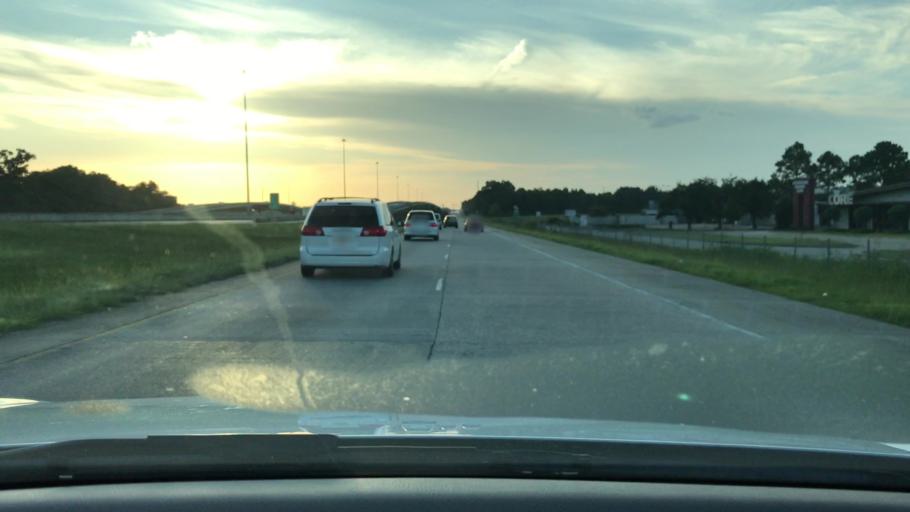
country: US
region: Louisiana
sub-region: East Baton Rouge Parish
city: Village Saint George
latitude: 30.3842
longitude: -91.0681
